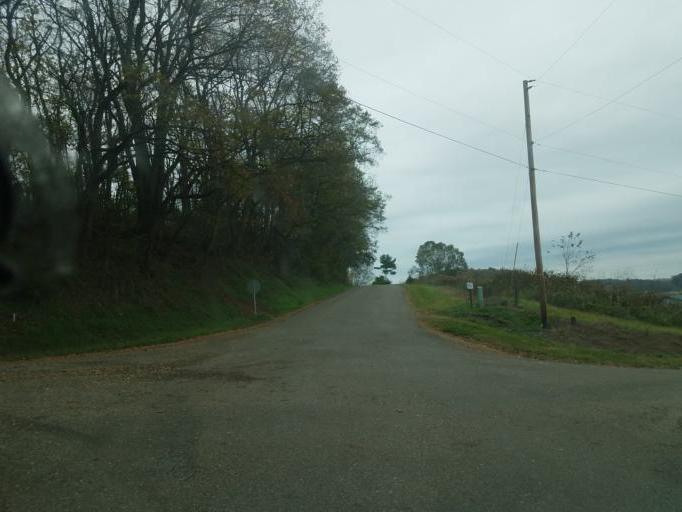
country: US
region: Ohio
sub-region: Ashland County
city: Loudonville
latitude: 40.6550
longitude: -82.2104
